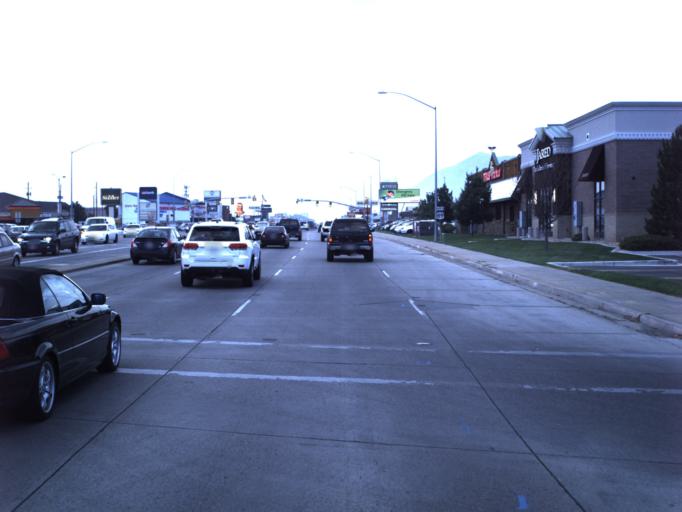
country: US
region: Utah
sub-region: Utah County
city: Orem
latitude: 40.2735
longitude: -111.6845
